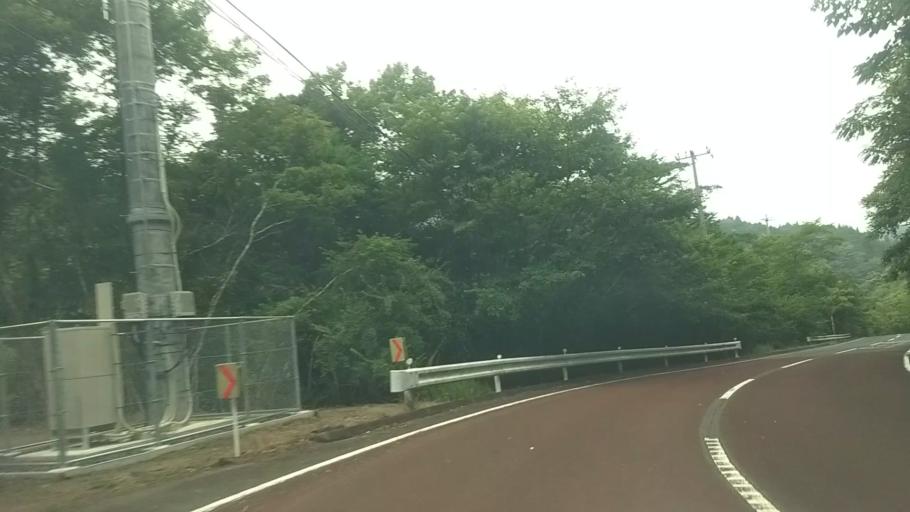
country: JP
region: Chiba
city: Kawaguchi
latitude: 35.1922
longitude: 140.1382
